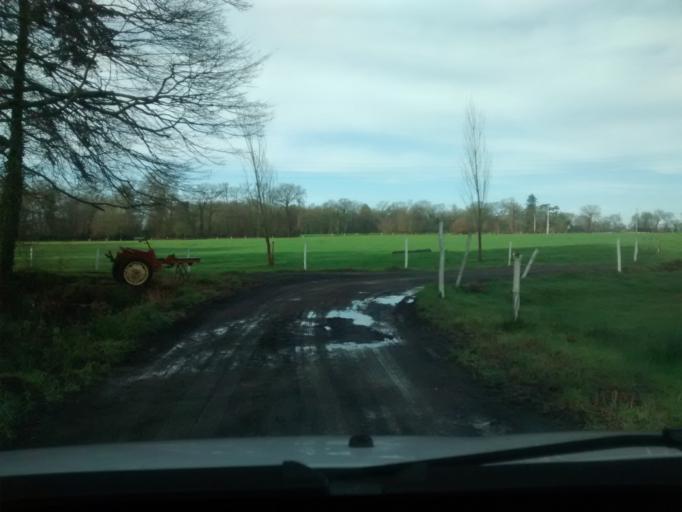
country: FR
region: Brittany
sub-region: Departement d'Ille-et-Vilaine
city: Vezin-le-Coquet
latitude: 48.1279
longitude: -1.7299
